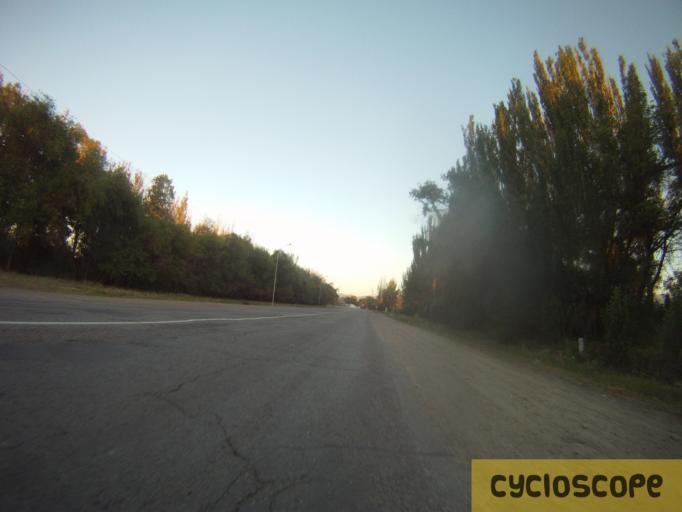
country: KZ
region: Almaty Oblysy
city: Turgen'
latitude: 43.5624
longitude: 78.3554
